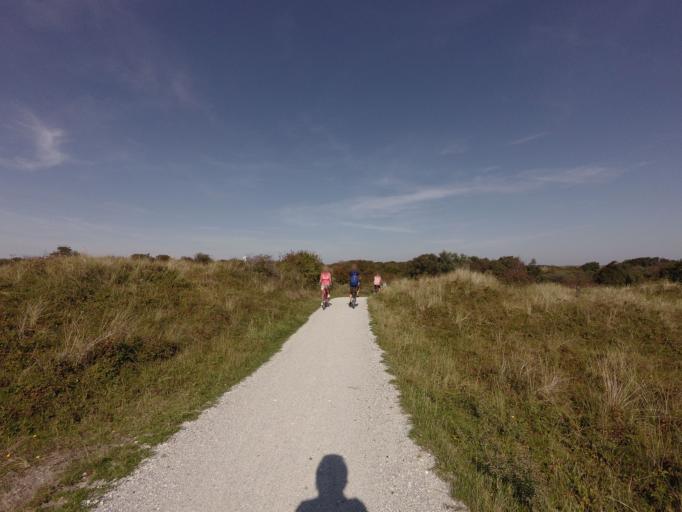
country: NL
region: Friesland
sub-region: Gemeente Schiermonnikoog
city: Schiermonnikoog
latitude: 53.4762
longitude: 6.1386
